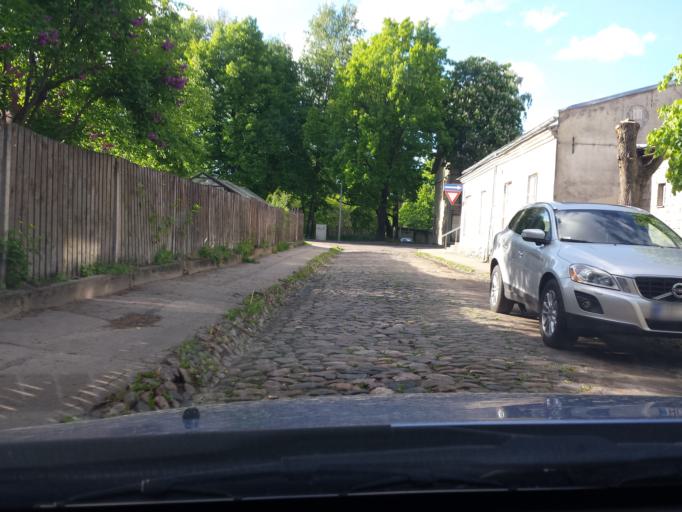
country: LV
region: Riga
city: Jaunciems
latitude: 56.9824
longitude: 24.1694
